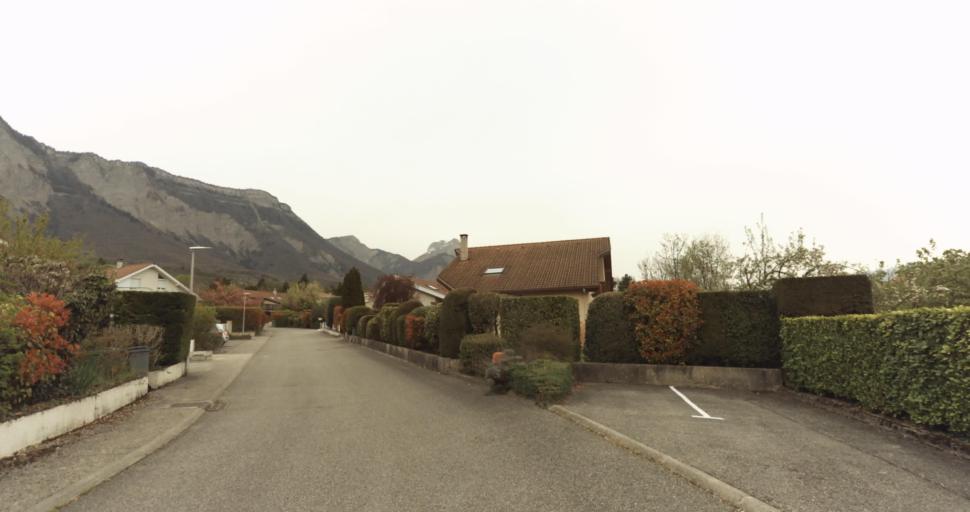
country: FR
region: Rhone-Alpes
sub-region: Departement de l'Isere
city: Biviers
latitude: 45.2354
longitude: 5.8152
